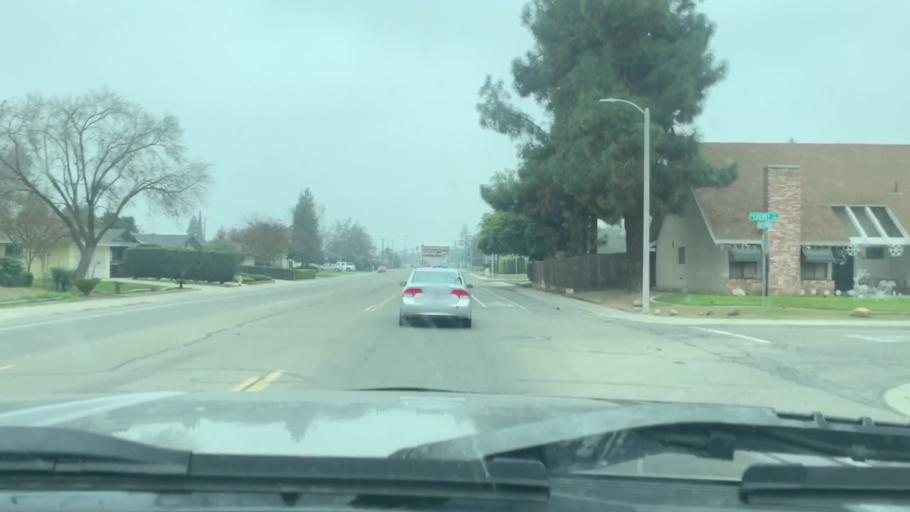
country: US
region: California
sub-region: Tulare County
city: Visalia
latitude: 36.3080
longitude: -119.3228
